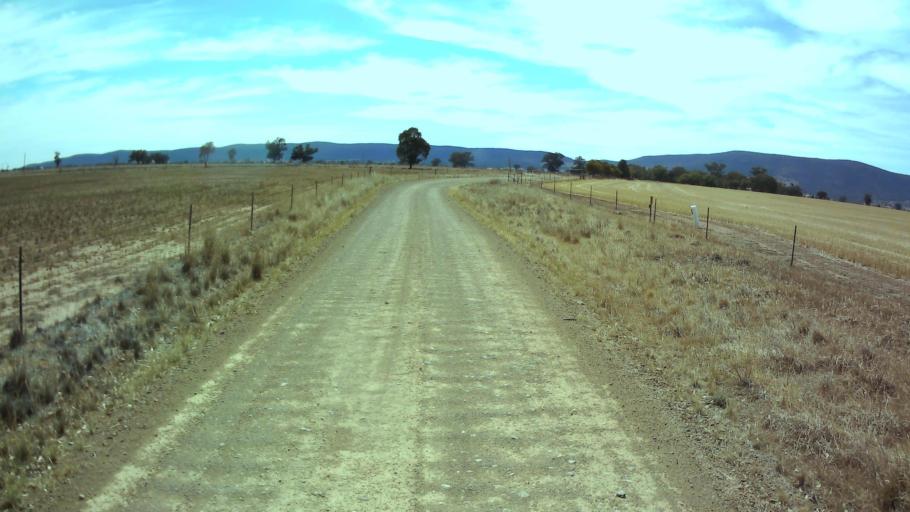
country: AU
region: New South Wales
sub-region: Weddin
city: Grenfell
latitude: -33.7206
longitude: 148.2552
